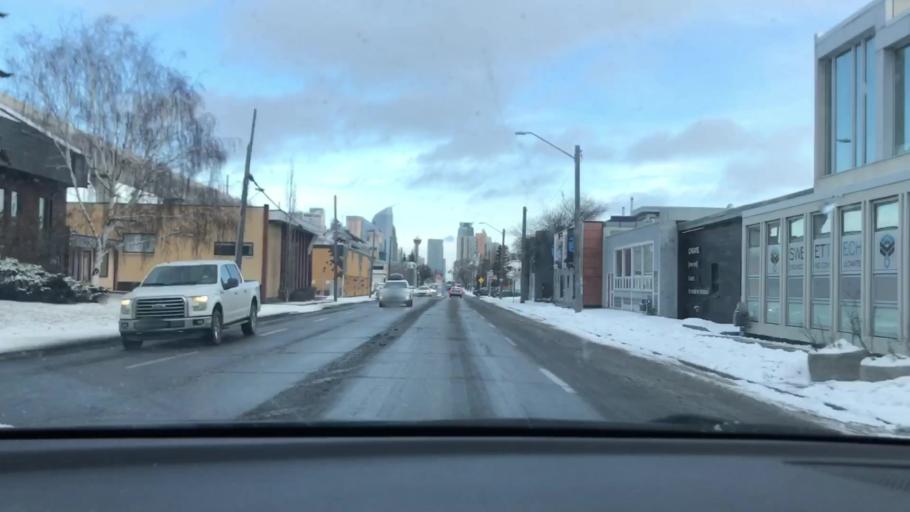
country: CA
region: Alberta
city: Calgary
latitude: 51.0445
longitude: -114.1060
